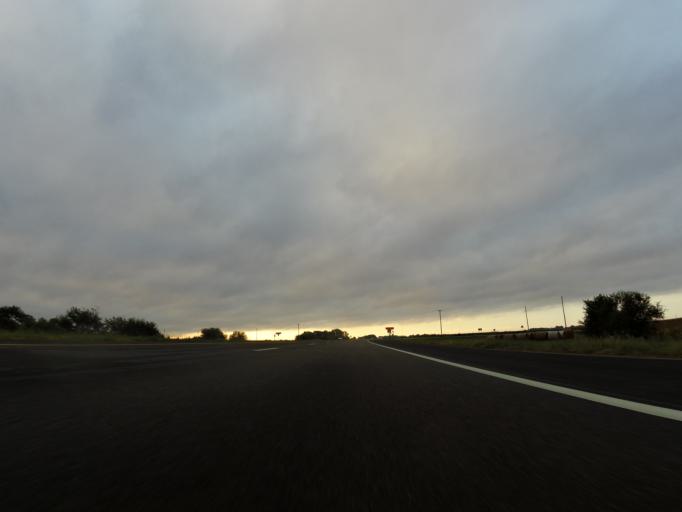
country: US
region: Kansas
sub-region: Sedgwick County
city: Colwich
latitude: 37.8404
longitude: -97.5745
